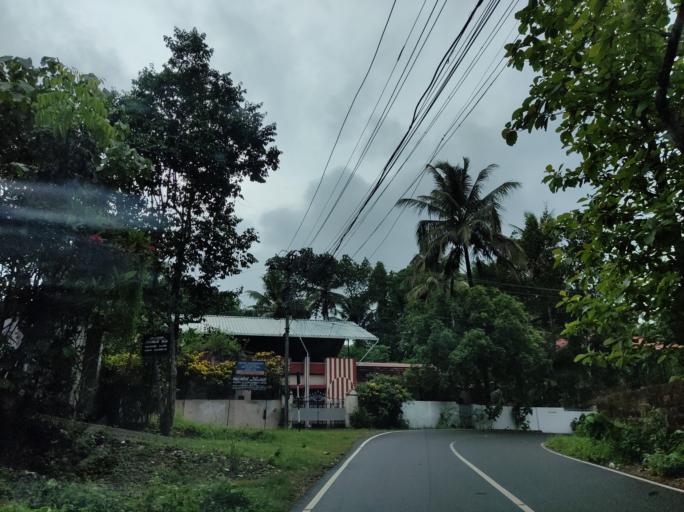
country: IN
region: Kerala
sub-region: Alappuzha
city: Mavelikara
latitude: 9.2334
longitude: 76.5615
